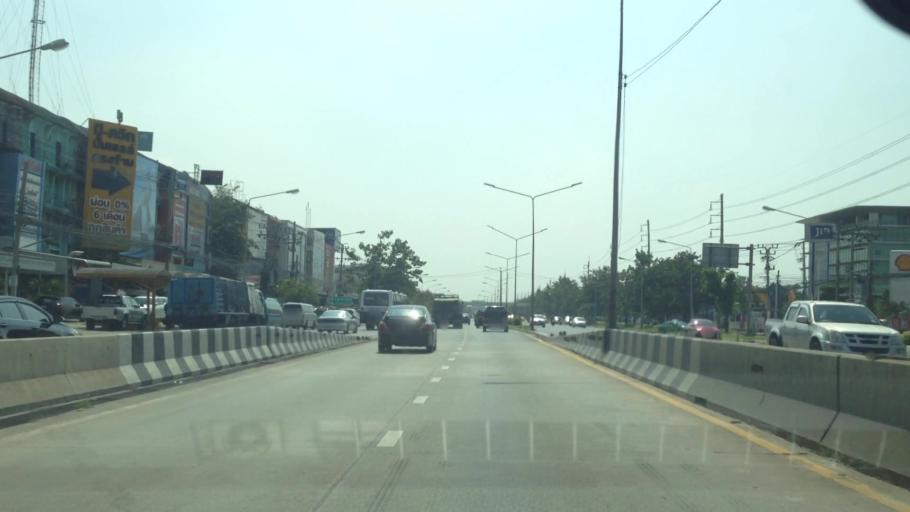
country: TH
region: Bangkok
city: Sai Mai
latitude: 13.9437
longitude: 100.6236
